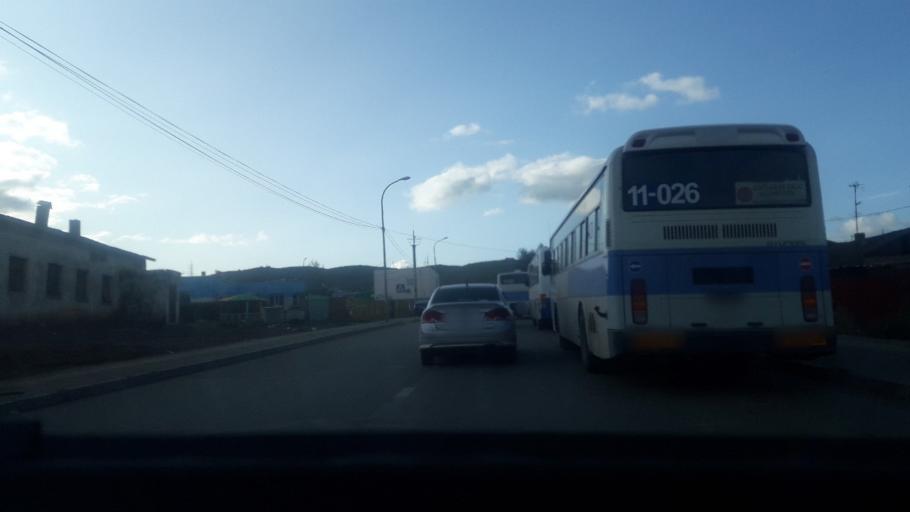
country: MN
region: Ulaanbaatar
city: Ulaanbaatar
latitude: 47.9338
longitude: 107.0069
